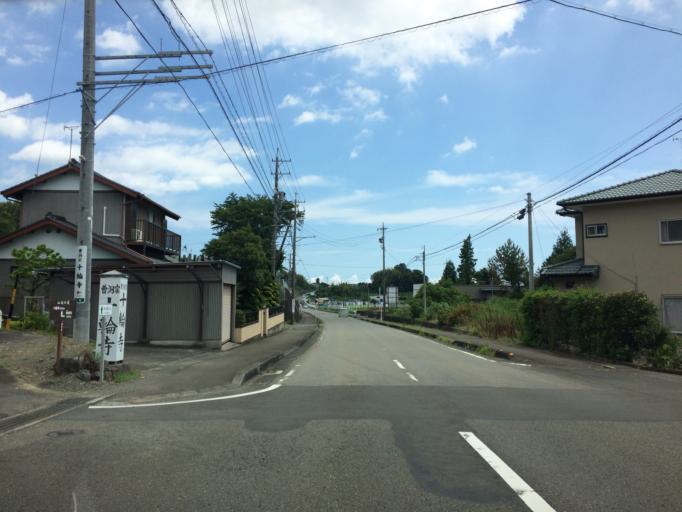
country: JP
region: Shizuoka
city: Yaizu
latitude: 34.9009
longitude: 138.2970
